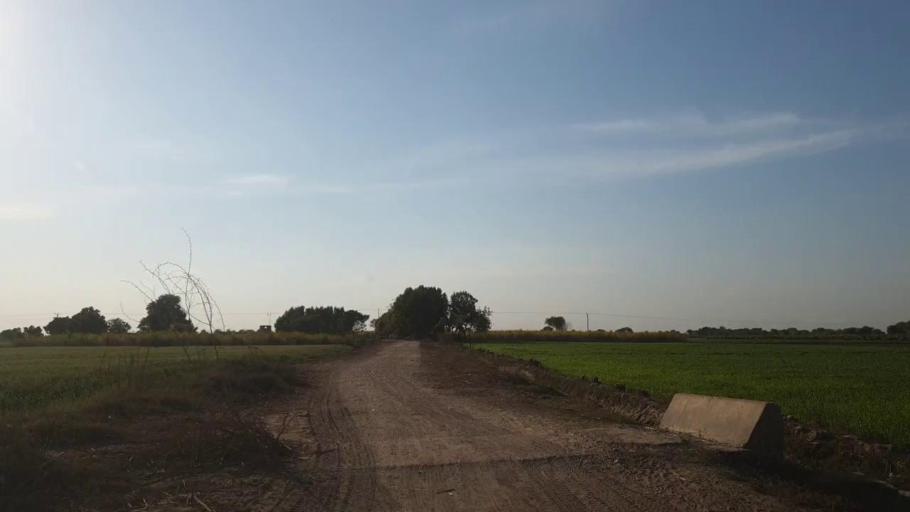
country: PK
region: Sindh
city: Tando Adam
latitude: 25.6942
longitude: 68.7150
